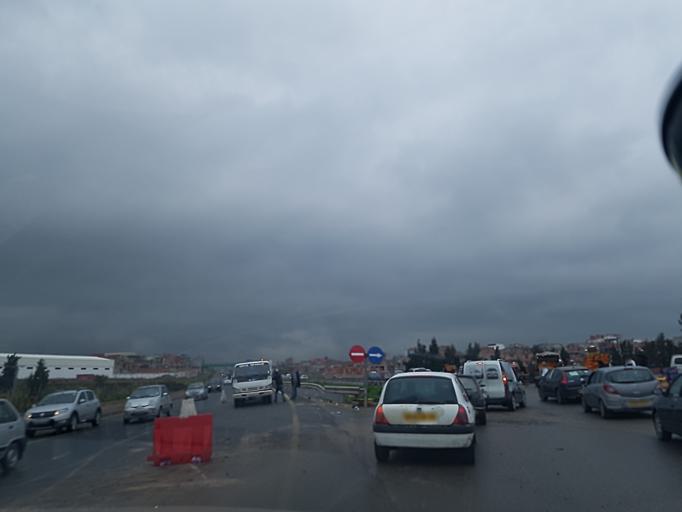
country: DZ
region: Boumerdes
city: Ouled Moussa
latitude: 36.6740
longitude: 3.3758
